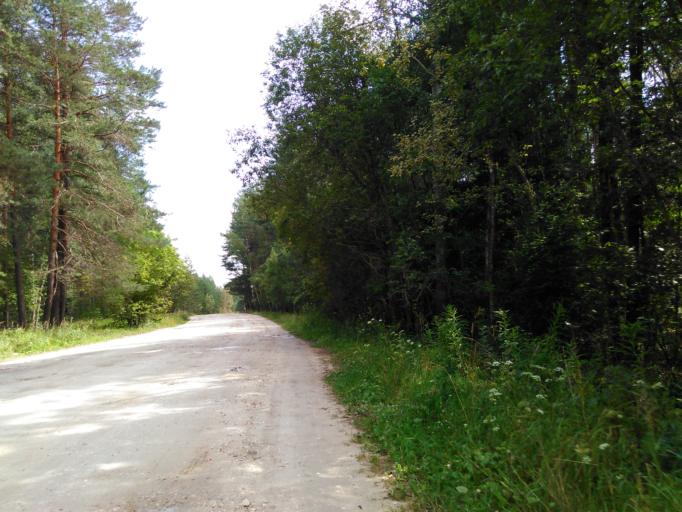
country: RU
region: Vladimir
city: Krasnyy Oktyabr'
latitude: 56.0071
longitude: 38.8303
